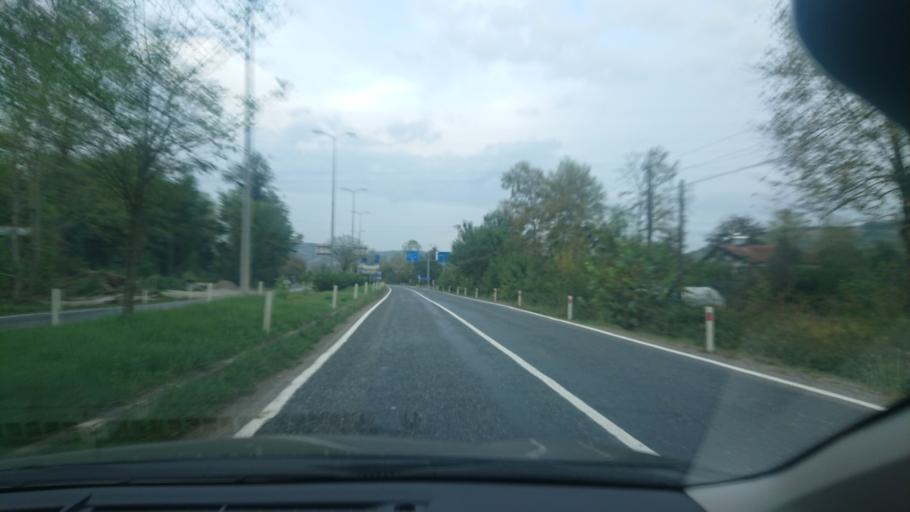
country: TR
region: Zonguldak
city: Gokcebey
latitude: 41.2996
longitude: 32.1214
